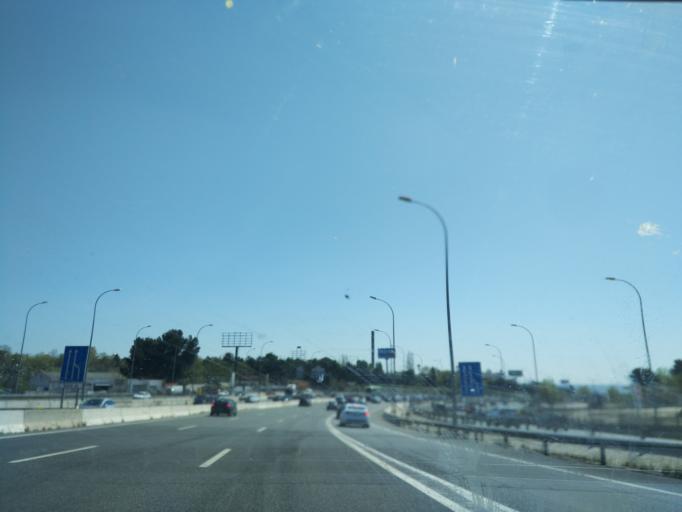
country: ES
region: Madrid
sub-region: Provincia de Madrid
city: Villa de Vallecas
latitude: 40.3578
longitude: -3.5568
